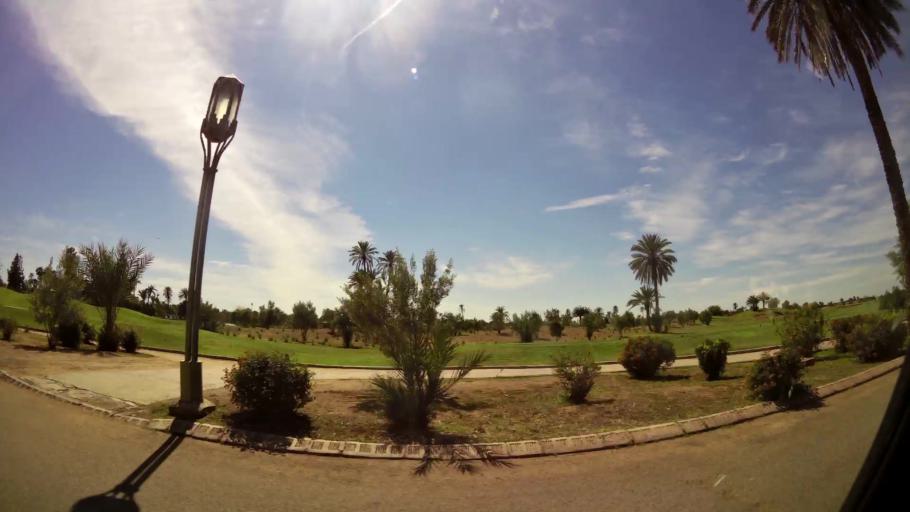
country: MA
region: Marrakech-Tensift-Al Haouz
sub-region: Marrakech
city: Marrakesh
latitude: 31.6141
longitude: -7.9346
